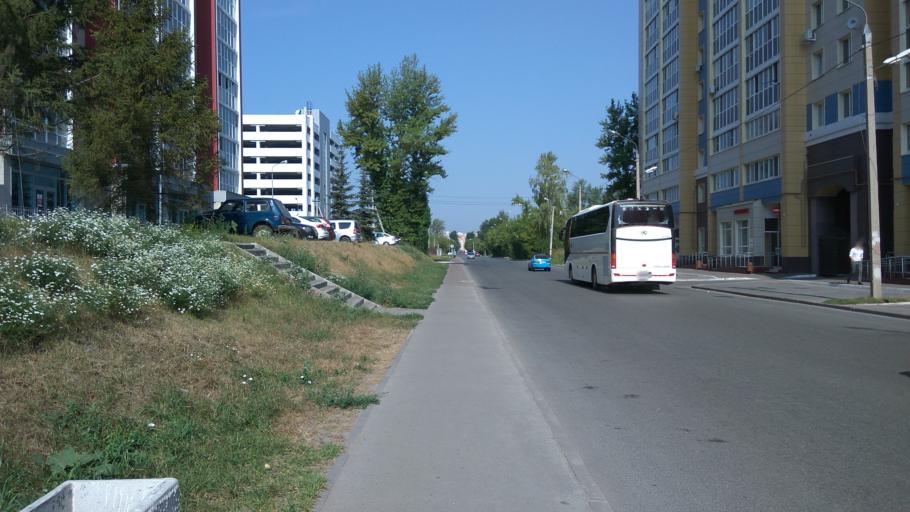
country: RU
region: Tatarstan
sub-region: Gorod Kazan'
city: Kazan
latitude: 55.7688
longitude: 49.1529
